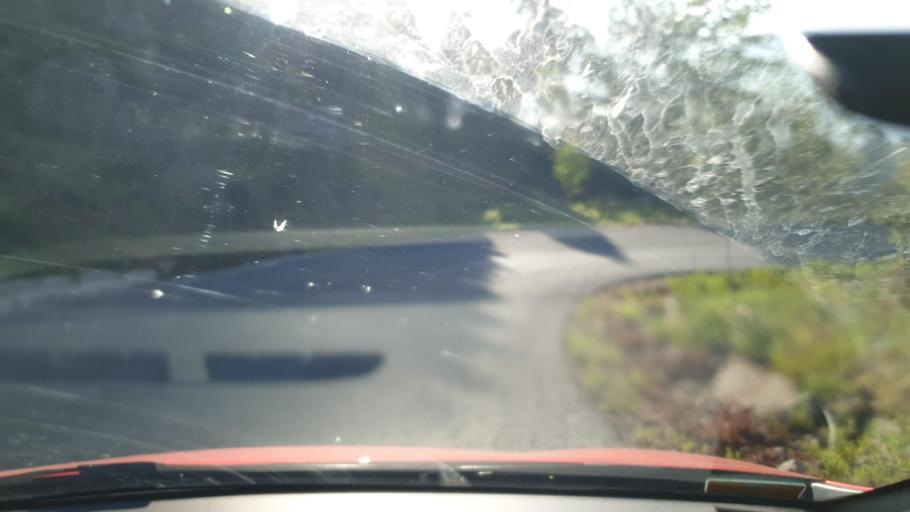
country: GR
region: Central Greece
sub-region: Nomos Evvoias
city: Yimnon
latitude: 38.6035
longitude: 23.9180
